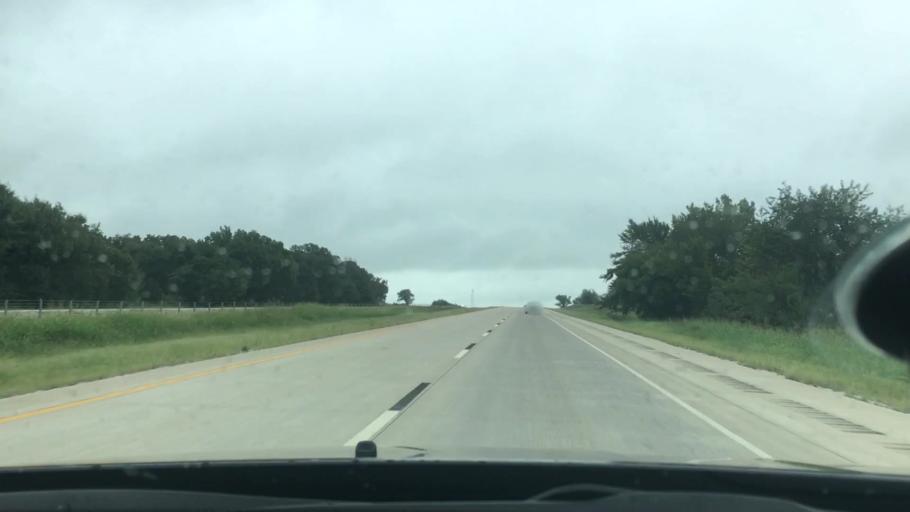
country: US
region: Oklahoma
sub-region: Okmulgee County
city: Wilson
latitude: 35.4275
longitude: -96.0782
